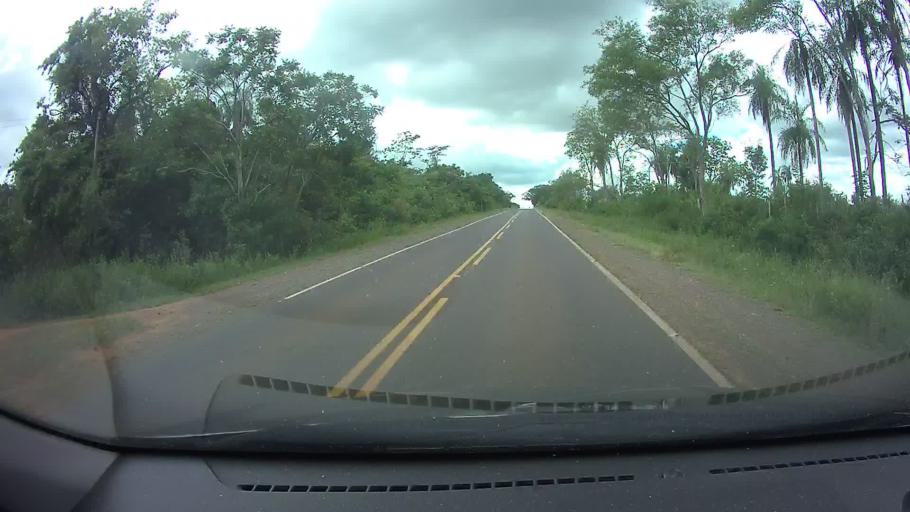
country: PY
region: Paraguari
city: Acahay
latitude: -25.9129
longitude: -57.0608
